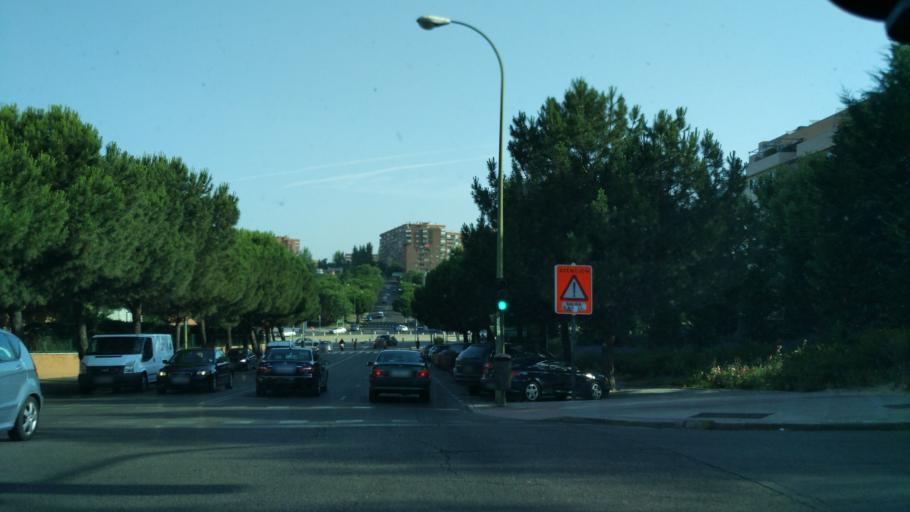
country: ES
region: Madrid
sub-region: Provincia de Madrid
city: Tetuan de las Victorias
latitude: 40.4743
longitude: -3.7208
